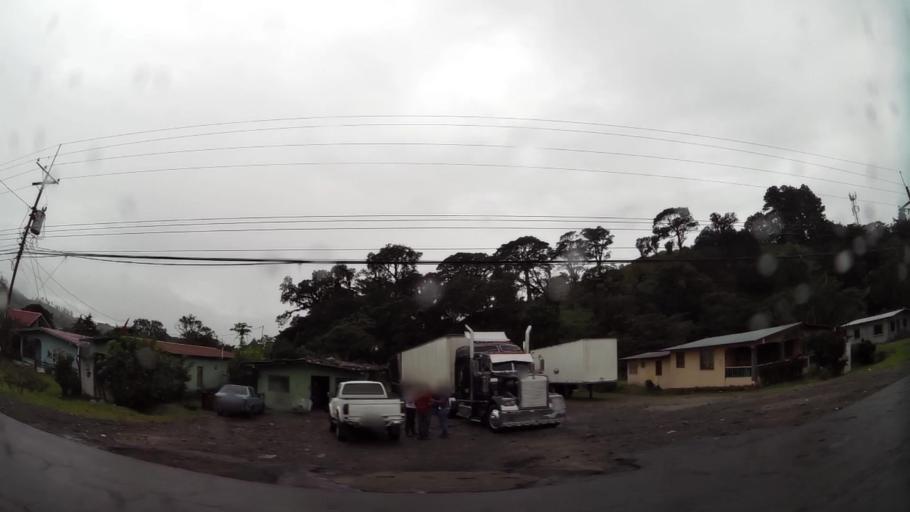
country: PA
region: Chiriqui
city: Volcan
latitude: 8.7738
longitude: -82.6380
